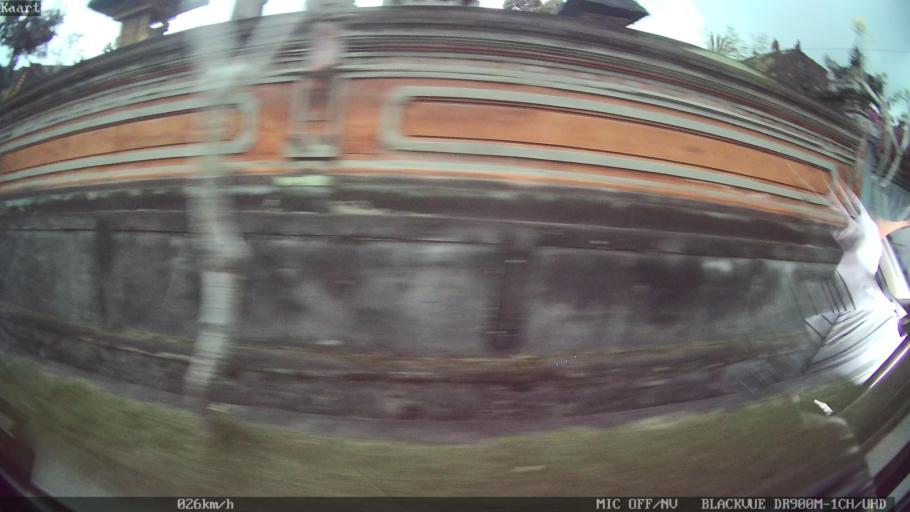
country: ID
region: Bali
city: Petang
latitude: -8.4139
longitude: 115.2239
